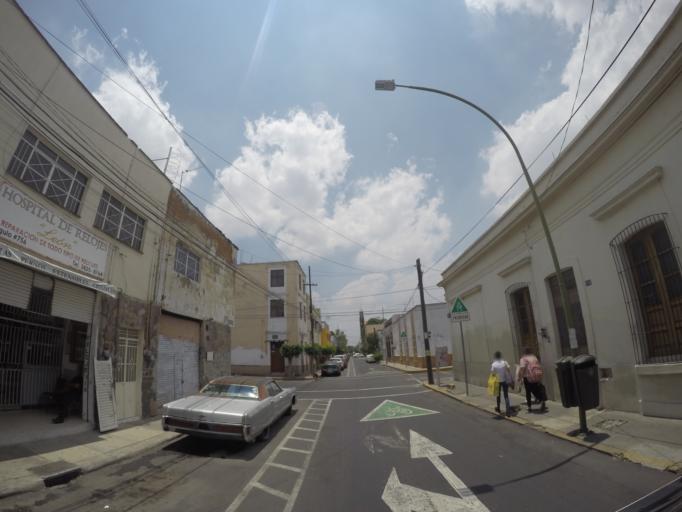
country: MX
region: Jalisco
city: Guadalajara
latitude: 20.6819
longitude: -103.3555
